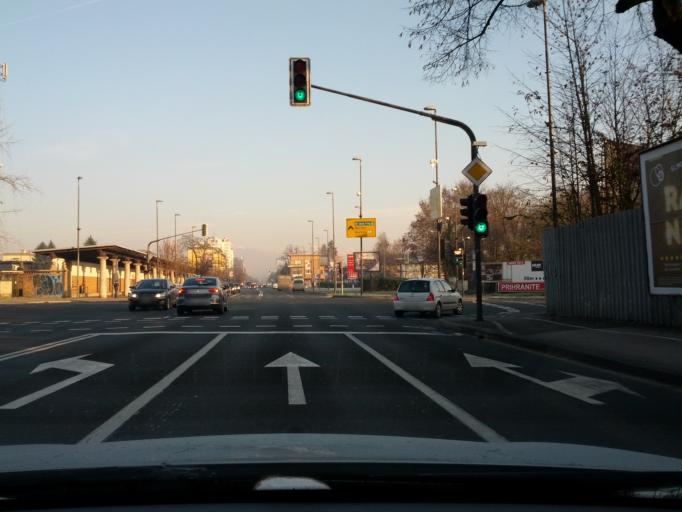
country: SI
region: Ljubljana
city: Ljubljana
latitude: 46.0675
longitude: 14.5099
